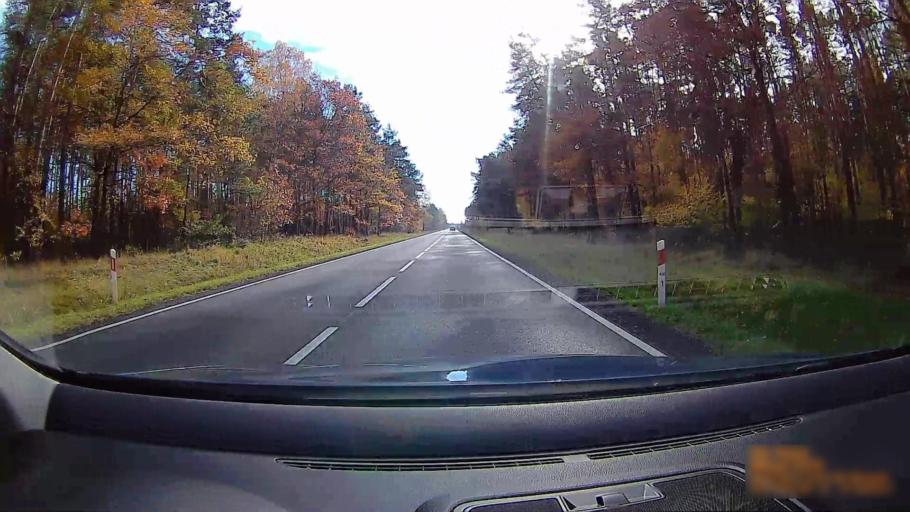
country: PL
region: Greater Poland Voivodeship
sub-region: Powiat ostrzeszowski
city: Ostrzeszow
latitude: 51.4520
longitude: 17.9068
